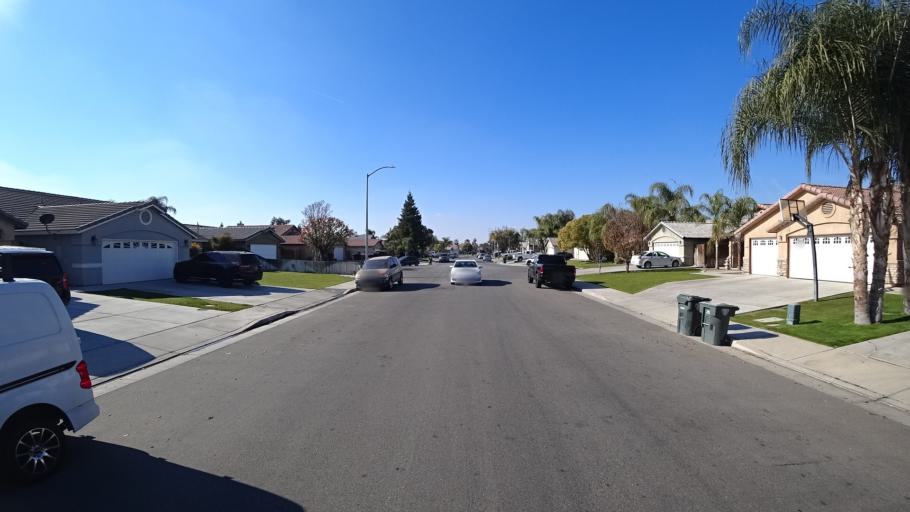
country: US
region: California
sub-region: Kern County
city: Greenfield
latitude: 35.2915
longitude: -119.0432
